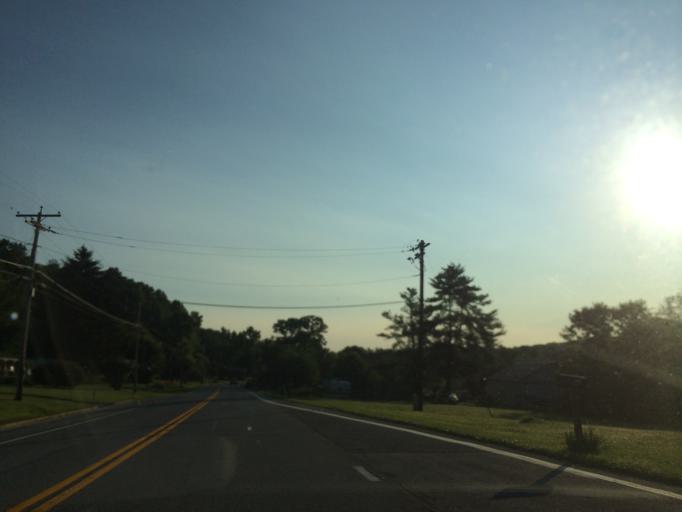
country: US
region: Maryland
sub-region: Carroll County
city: Manchester
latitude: 39.6934
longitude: -76.8755
